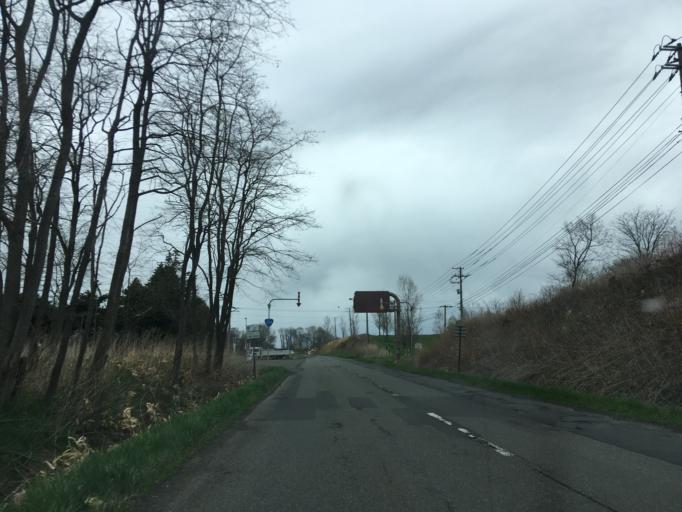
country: JP
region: Hokkaido
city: Chitose
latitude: 42.8964
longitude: 141.8136
